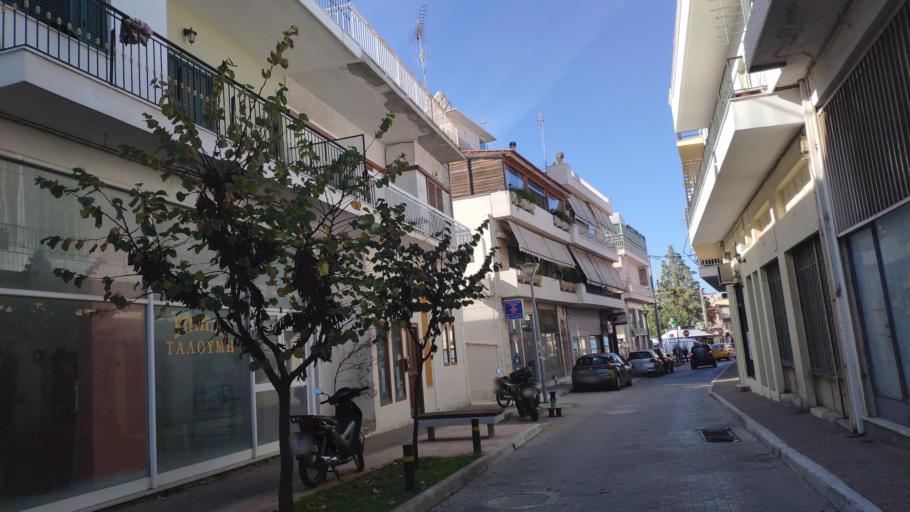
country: GR
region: Attica
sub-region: Nomarchia Athinas
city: Metamorfosi
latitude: 38.0615
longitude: 23.7621
